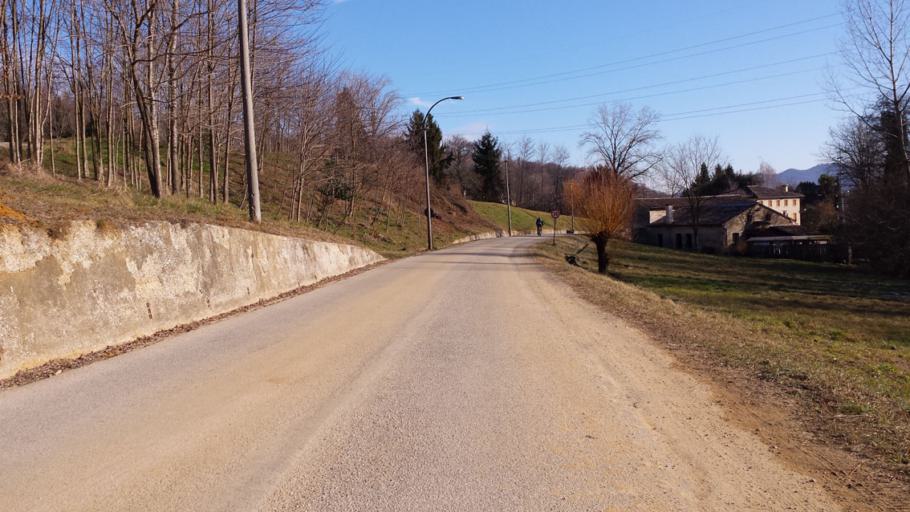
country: IT
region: Veneto
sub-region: Provincia di Treviso
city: Castelcucco
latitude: 45.8354
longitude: 11.8746
